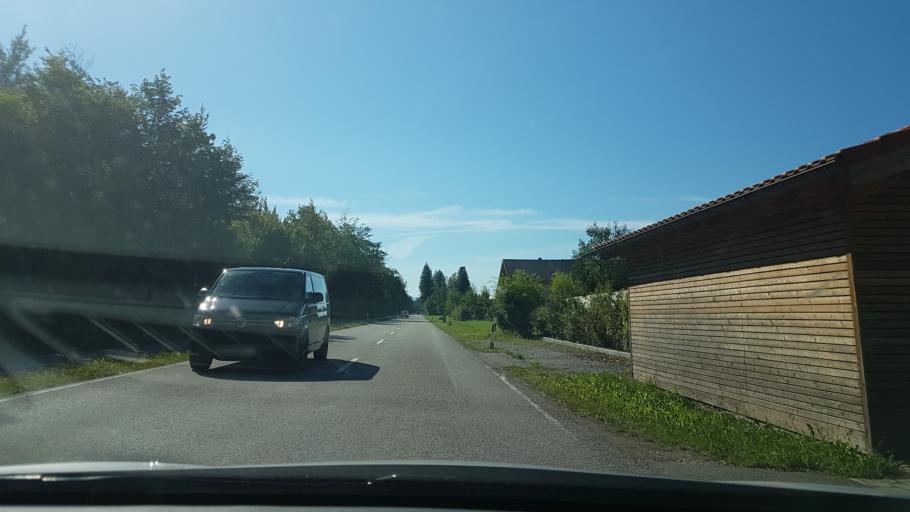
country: DE
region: Bavaria
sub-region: Upper Bavaria
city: Aying
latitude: 47.9472
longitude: 11.7516
